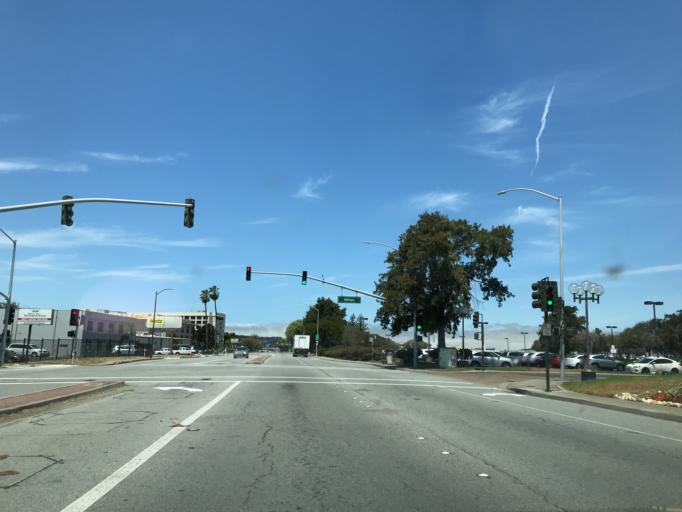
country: US
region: California
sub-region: San Mateo County
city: Millbrae
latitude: 37.6025
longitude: -122.3718
